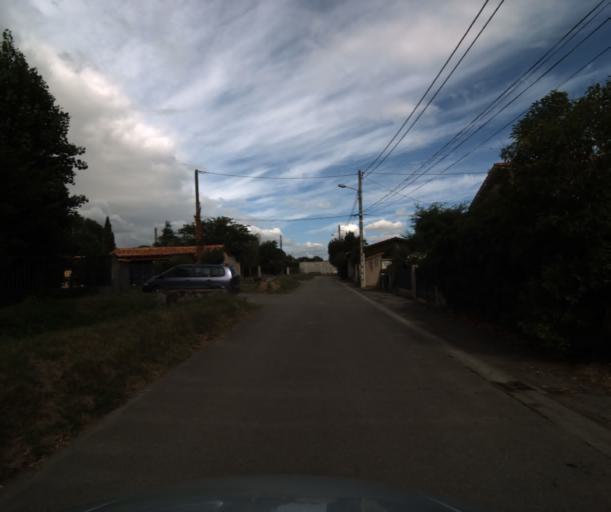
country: FR
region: Midi-Pyrenees
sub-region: Departement de la Haute-Garonne
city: Seysses
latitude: 43.4628
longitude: 1.3142
